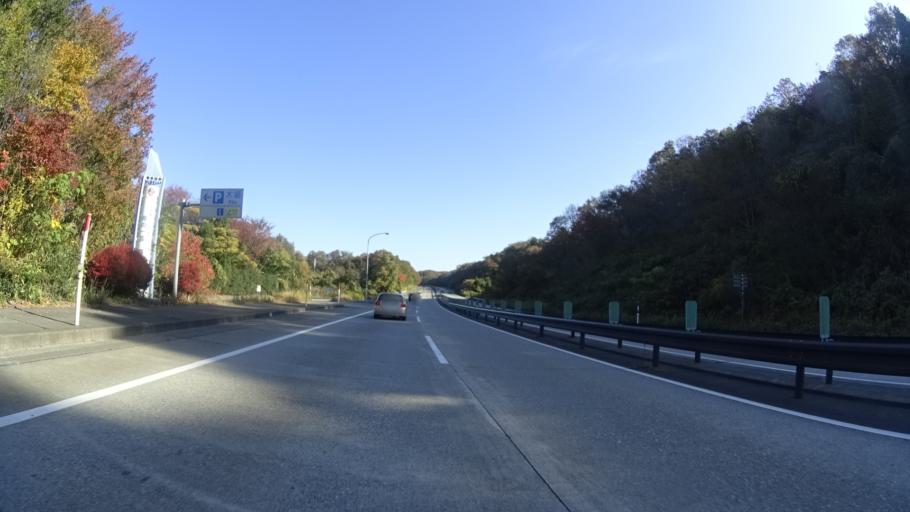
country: JP
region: Ishikawa
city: Komatsu
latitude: 36.3598
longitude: 136.4542
